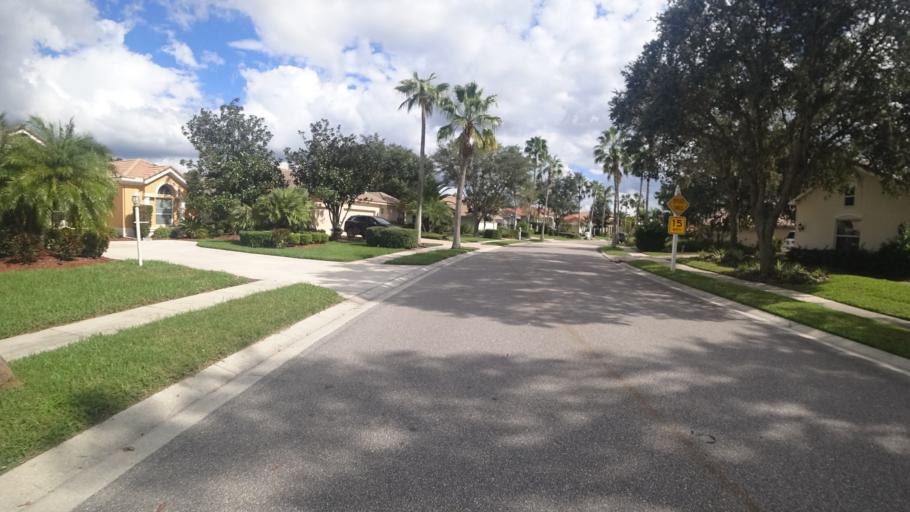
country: US
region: Florida
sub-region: Sarasota County
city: The Meadows
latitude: 27.4014
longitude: -82.4245
